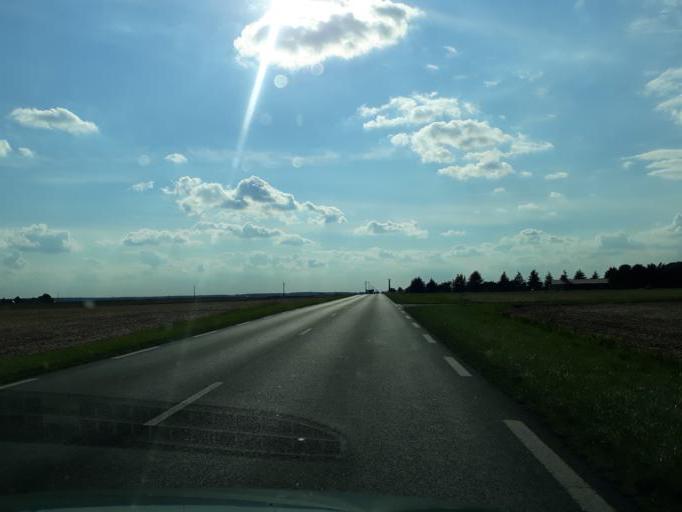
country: FR
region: Centre
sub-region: Departement du Loir-et-Cher
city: Ouzouer-le-Marche
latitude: 47.9042
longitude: 1.4402
